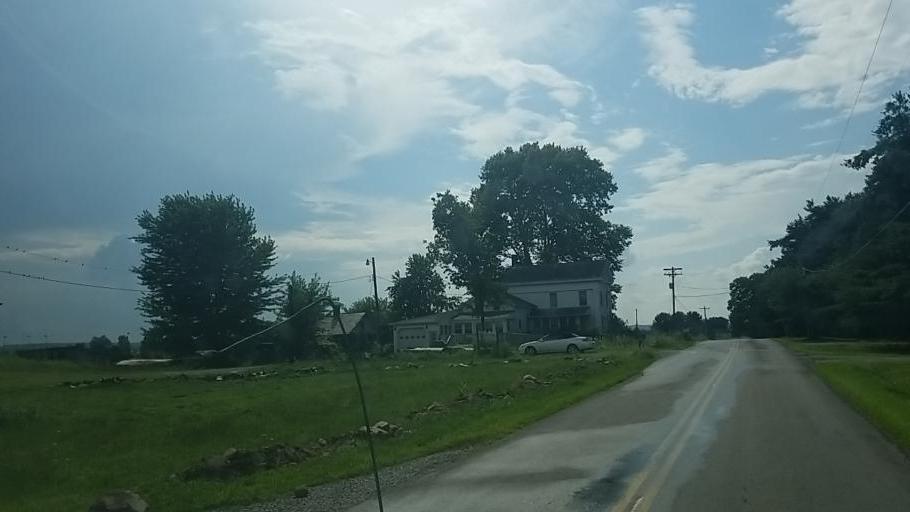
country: US
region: Ohio
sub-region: Medina County
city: Lodi
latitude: 41.0050
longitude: -81.9850
